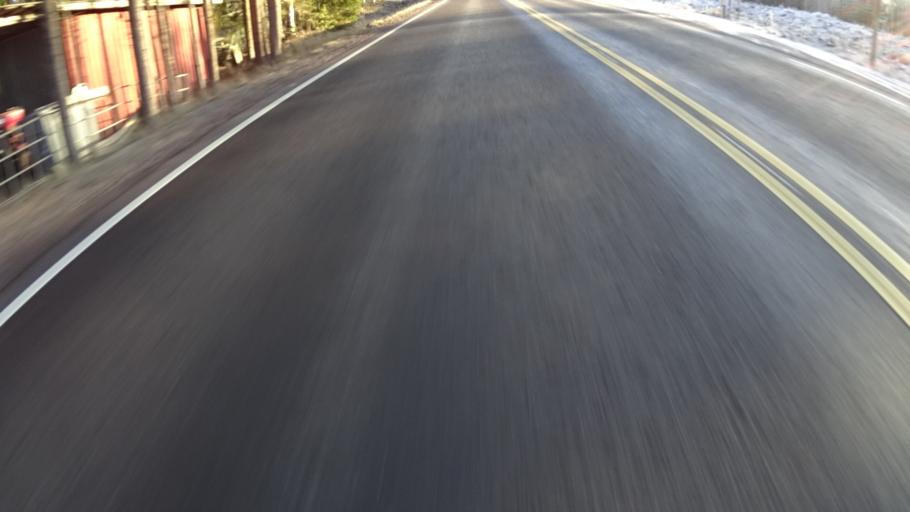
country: FI
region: Uusimaa
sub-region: Helsinki
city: Vihti
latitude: 60.5136
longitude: 24.4252
